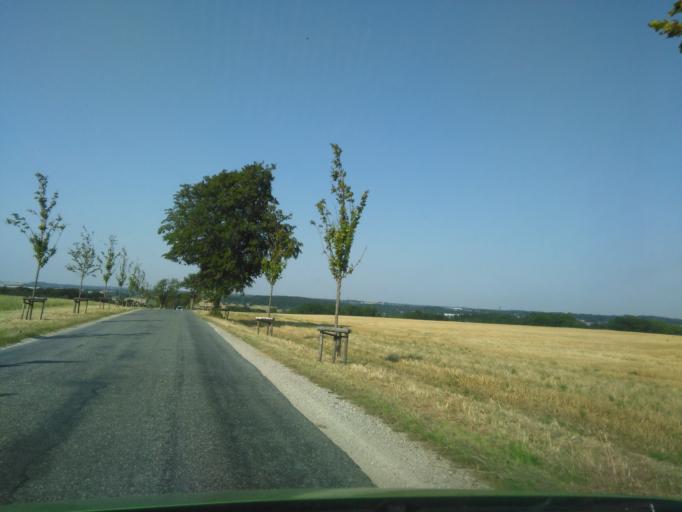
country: DK
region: Central Jutland
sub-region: Arhus Kommune
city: Kolt
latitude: 56.1306
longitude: 10.0792
